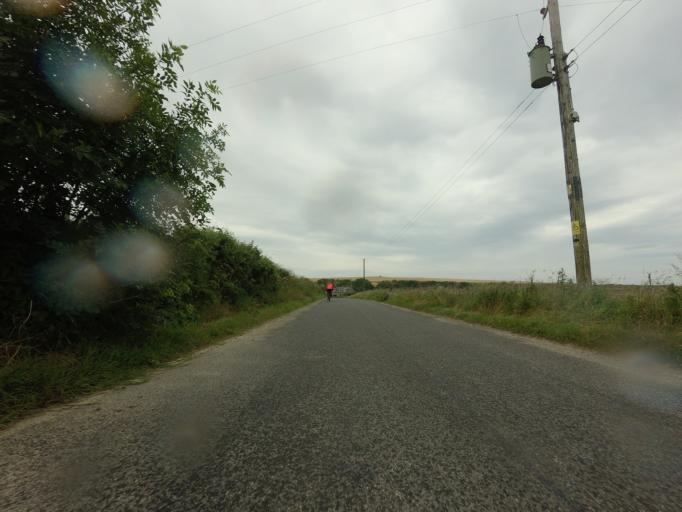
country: GB
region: Scotland
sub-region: Aberdeenshire
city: Portsoy
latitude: 57.6764
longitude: -2.6499
